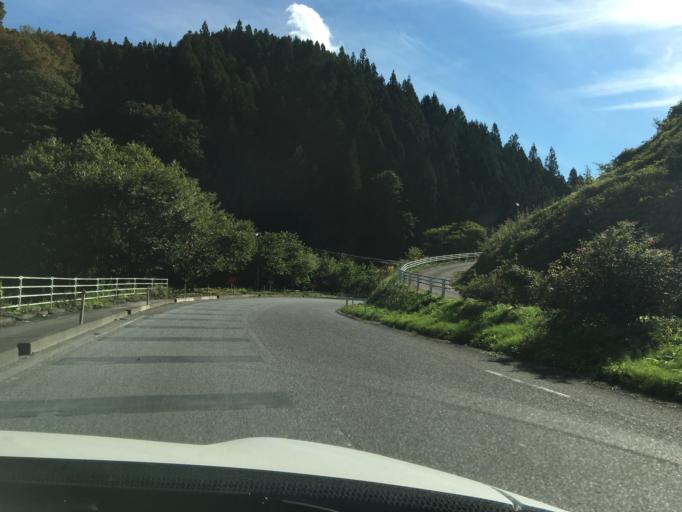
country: JP
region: Fukushima
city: Ishikawa
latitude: 37.1287
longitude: 140.5902
